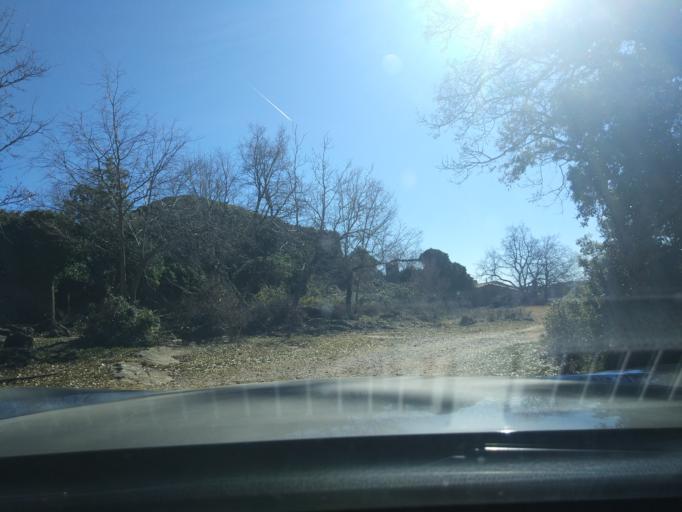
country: ES
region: Aragon
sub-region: Provincia de Huesca
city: Palo
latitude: 42.3118
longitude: 0.3410
